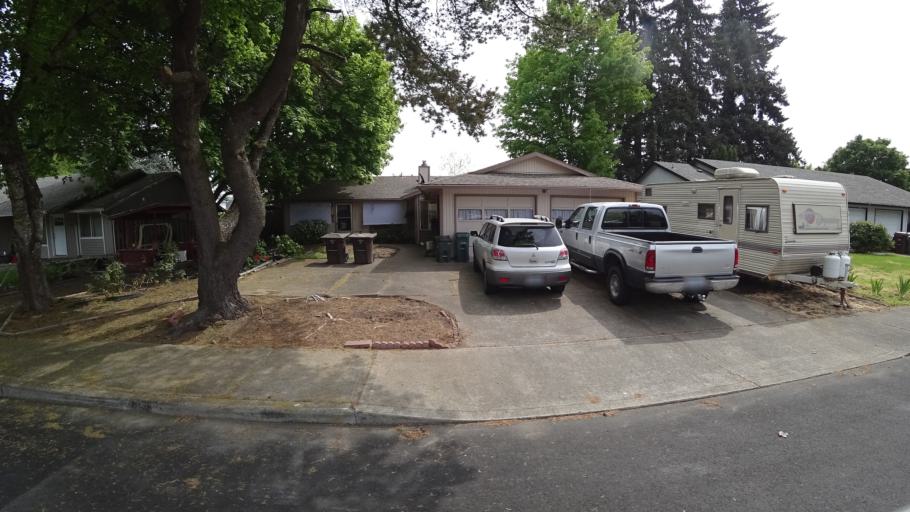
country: US
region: Oregon
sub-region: Washington County
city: Hillsboro
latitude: 45.5321
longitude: -122.9917
